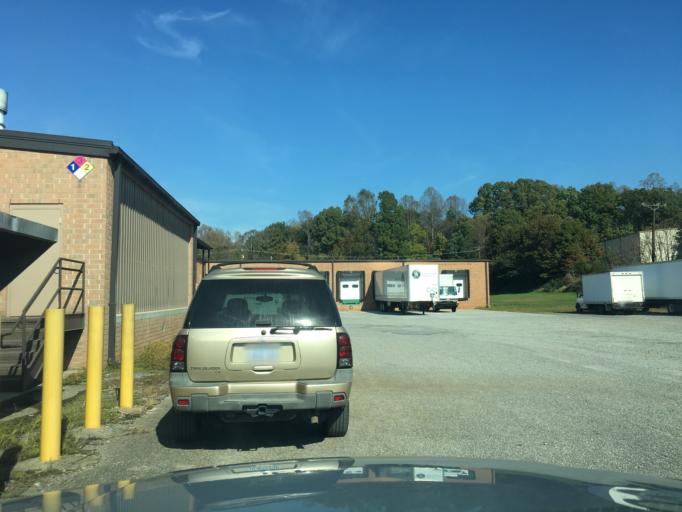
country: US
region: North Carolina
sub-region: Catawba County
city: Conover
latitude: 35.7134
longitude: -81.2447
